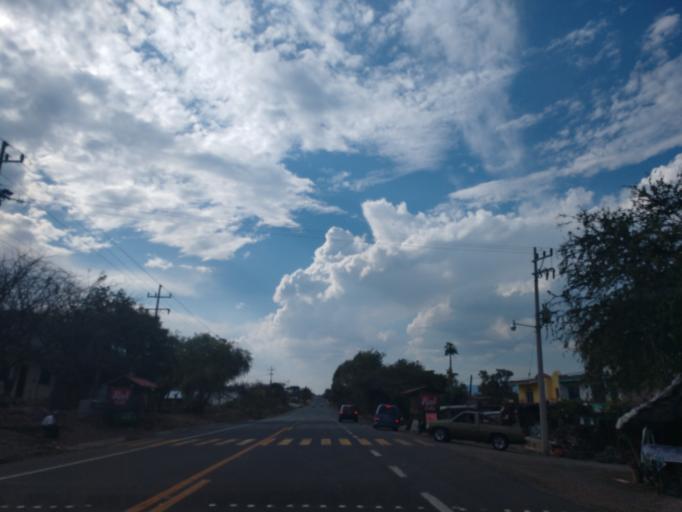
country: MX
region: Jalisco
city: Chapala
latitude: 20.1705
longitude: -103.2151
